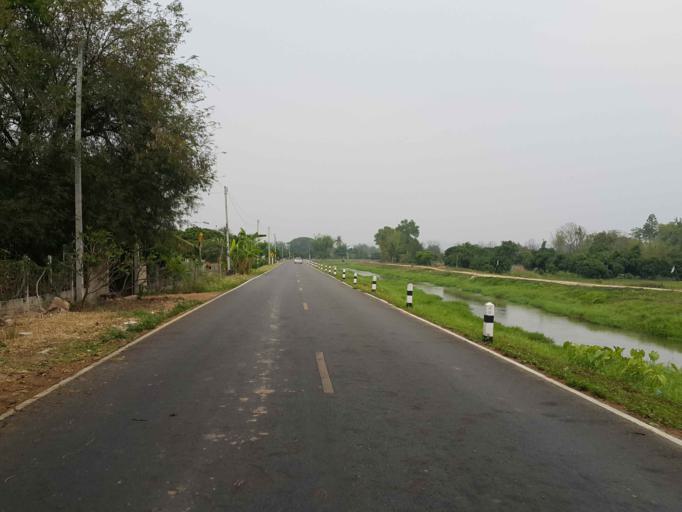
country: TH
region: Chiang Mai
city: Mae Taeng
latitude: 18.9873
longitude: 98.9792
